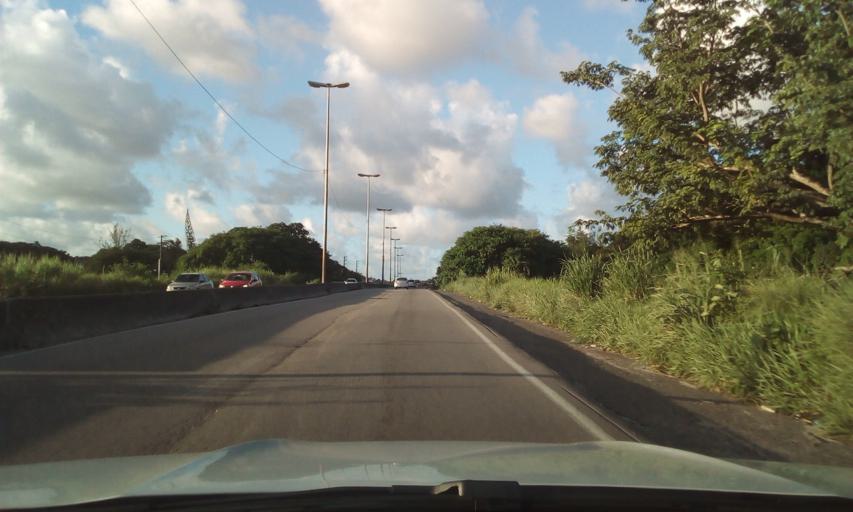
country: BR
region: Pernambuco
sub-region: Recife
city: Recife
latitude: -8.0181
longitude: -34.9417
